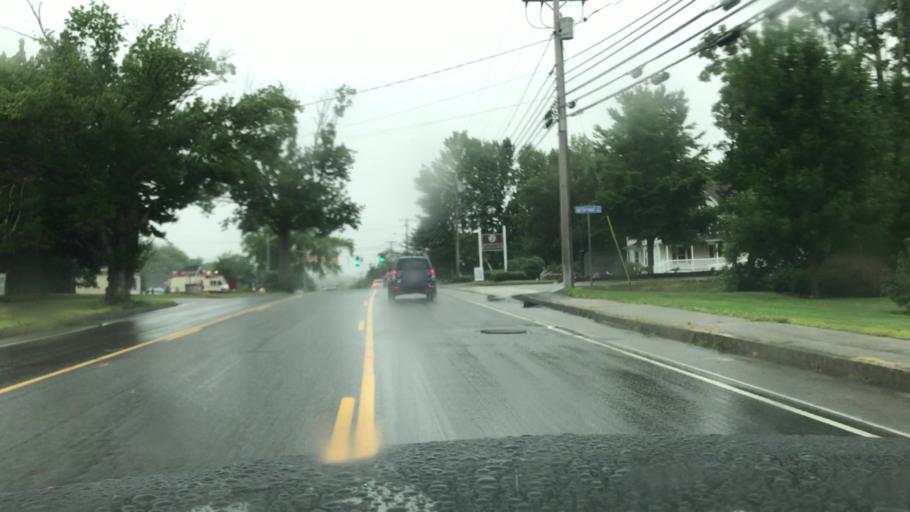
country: US
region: Maine
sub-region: York County
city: Kennebunk
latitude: 43.3984
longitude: -70.5292
